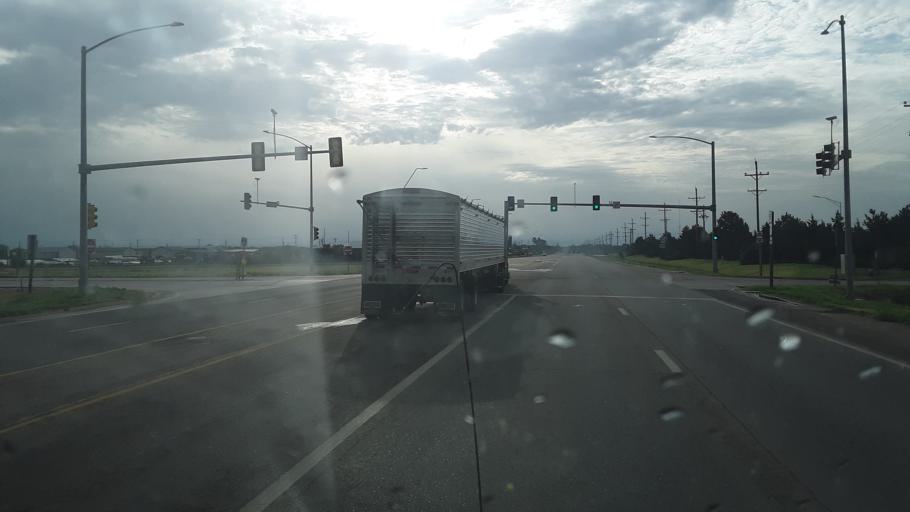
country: US
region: Kansas
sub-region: Finney County
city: Garden City
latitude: 37.9602
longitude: -100.8386
